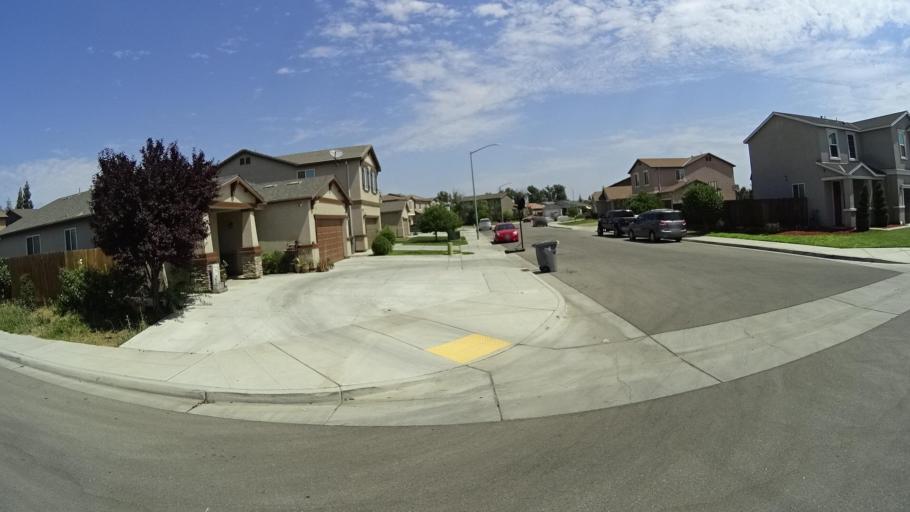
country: US
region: California
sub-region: Fresno County
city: Sunnyside
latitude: 36.7405
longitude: -119.6909
